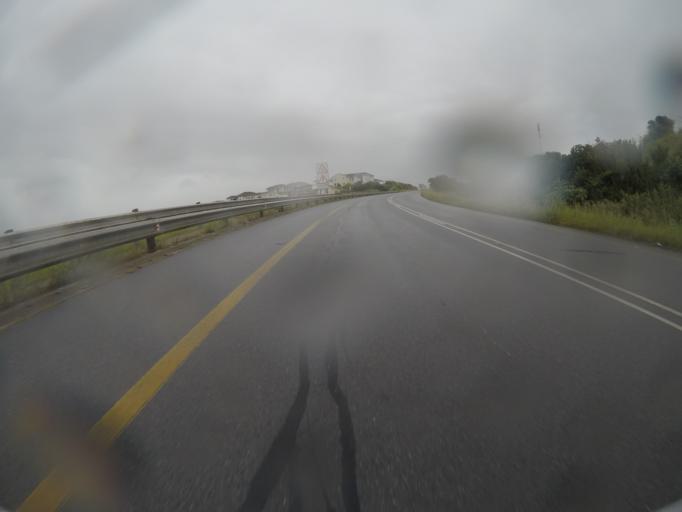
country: ZA
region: Eastern Cape
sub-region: Buffalo City Metropolitan Municipality
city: East London
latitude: -32.9539
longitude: 27.9142
